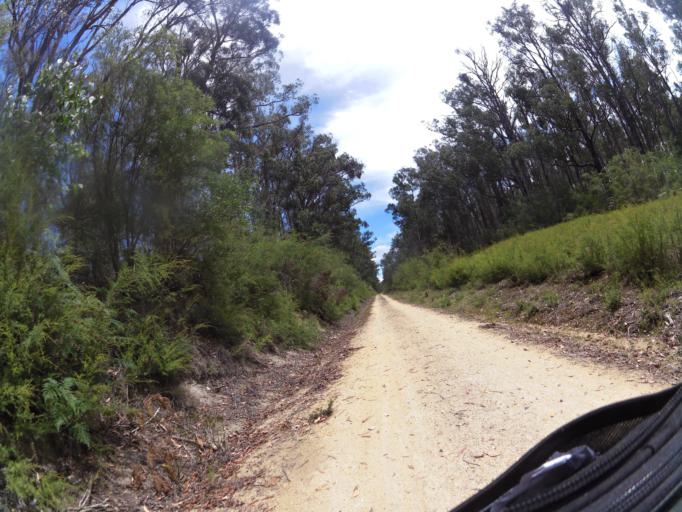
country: AU
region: Victoria
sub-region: East Gippsland
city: Lakes Entrance
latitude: -37.7416
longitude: 148.0292
